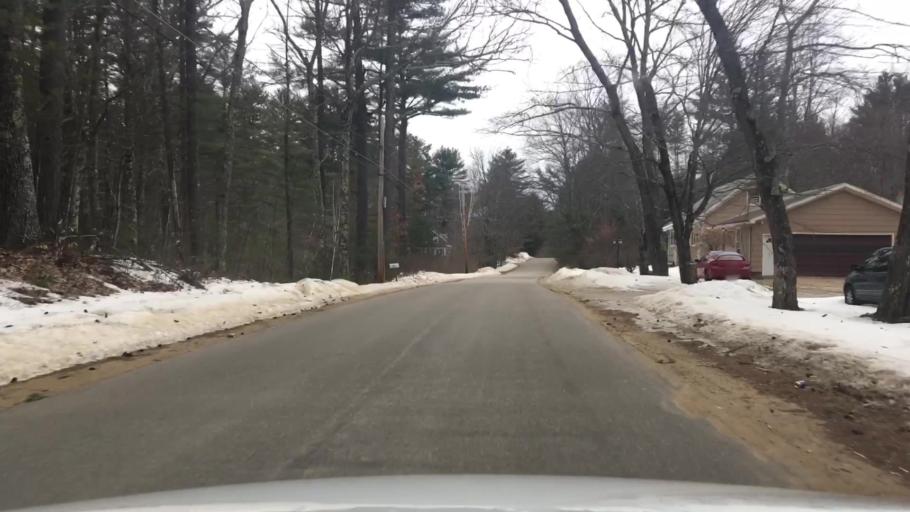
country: US
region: New Hampshire
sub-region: Strafford County
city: Rochester
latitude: 43.3565
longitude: -70.9670
